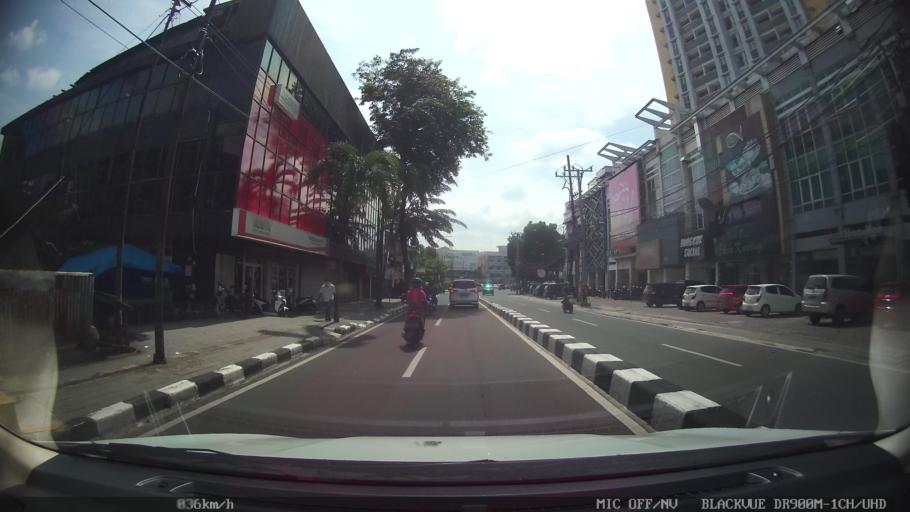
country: ID
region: North Sumatra
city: Medan
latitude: 3.5843
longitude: 98.6770
